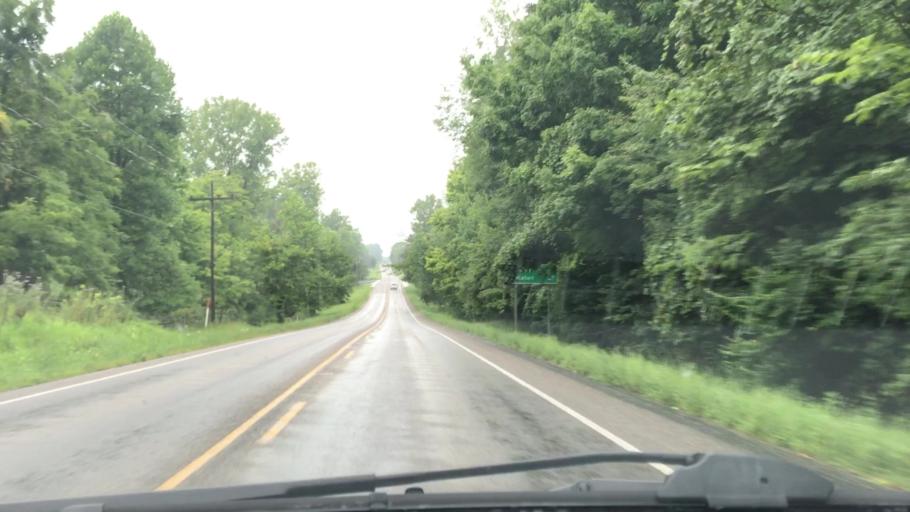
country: US
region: Indiana
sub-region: Hamilton County
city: Westfield
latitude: 40.0970
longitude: -86.1339
